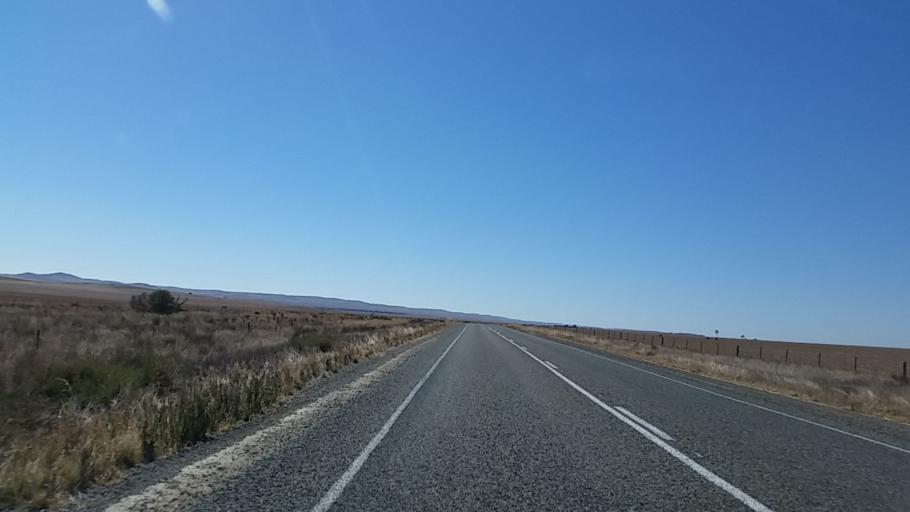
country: AU
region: South Australia
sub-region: Northern Areas
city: Jamestown
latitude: -33.2792
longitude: 138.8687
